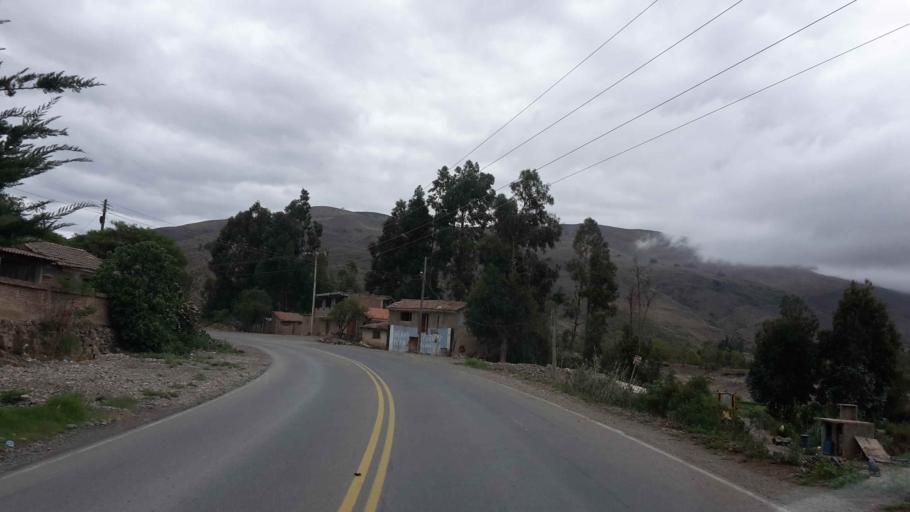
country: BO
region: Cochabamba
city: Punata
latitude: -17.5137
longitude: -65.8139
